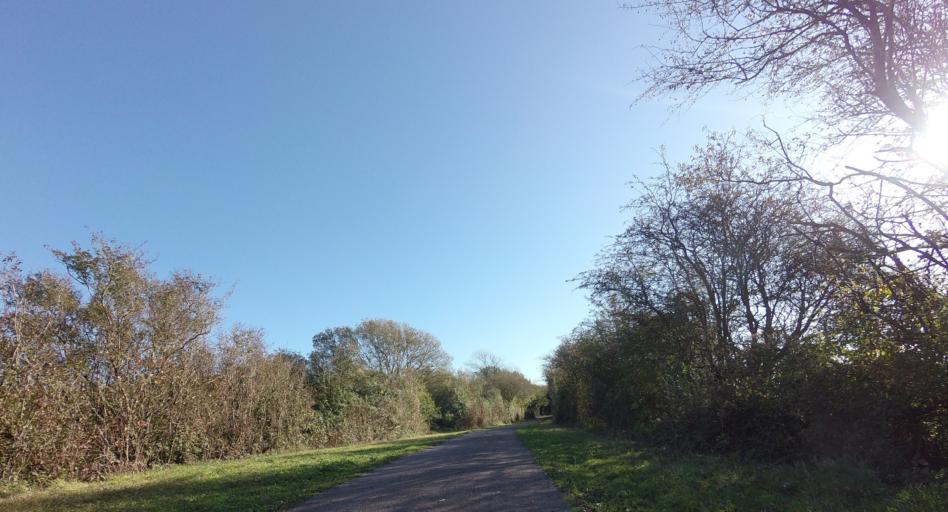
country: GB
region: England
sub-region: West Sussex
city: Shoreham-by-Sea
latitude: 50.8592
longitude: -0.2927
